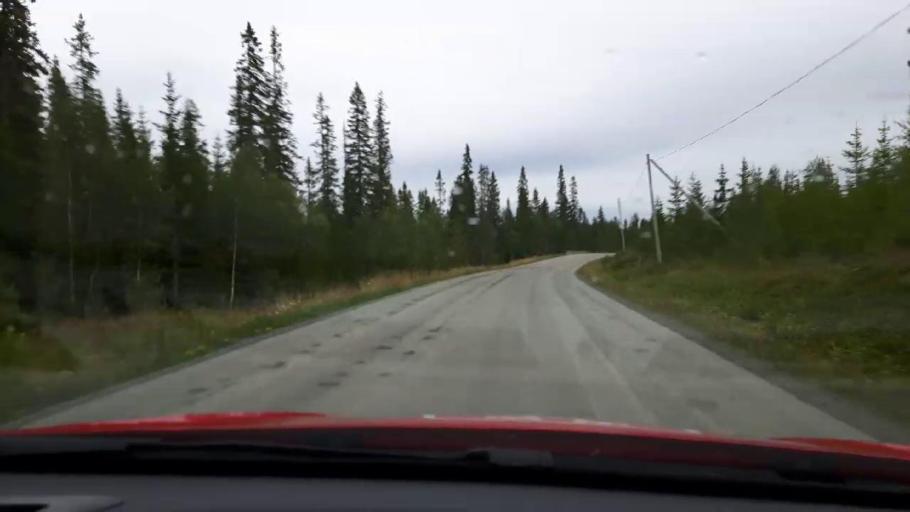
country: SE
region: Jaemtland
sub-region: Are Kommun
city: Jarpen
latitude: 63.4265
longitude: 13.3386
